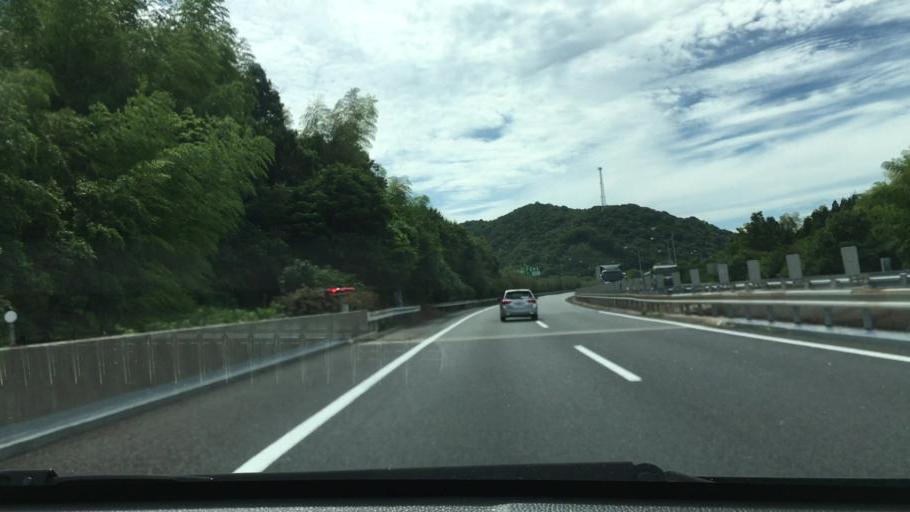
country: JP
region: Yamaguchi
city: Hofu
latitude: 34.0510
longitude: 131.5147
